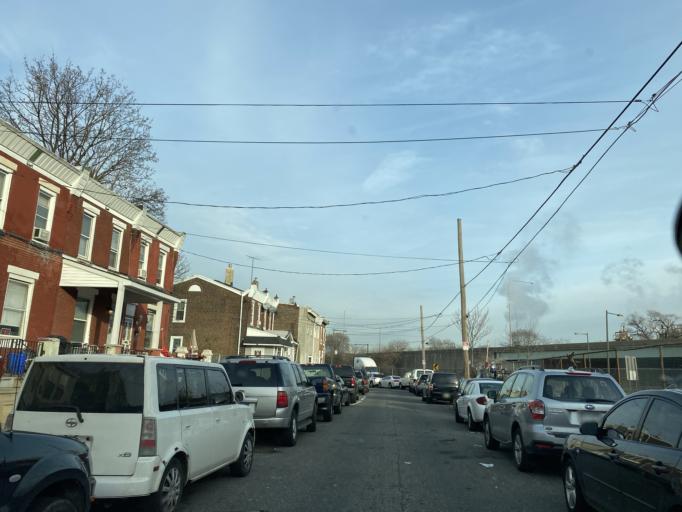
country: US
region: New Jersey
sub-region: Burlington County
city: Palmyra
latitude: 40.0072
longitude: -75.0748
